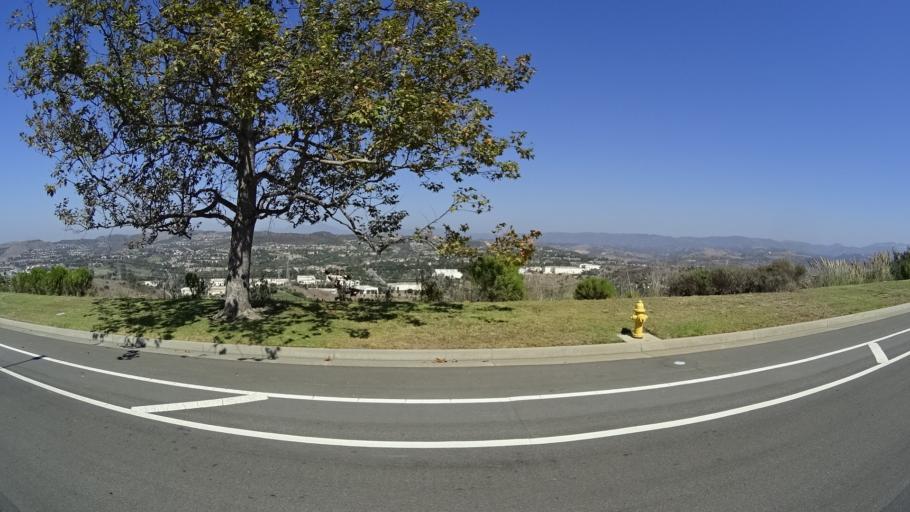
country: US
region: California
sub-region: Orange County
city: San Clemente
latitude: 33.4503
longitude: -117.5905
